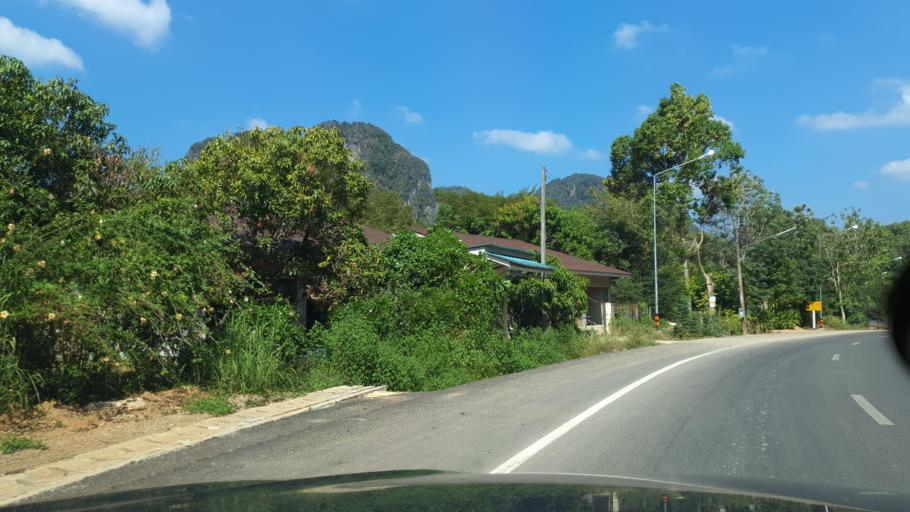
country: TH
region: Krabi
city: Krabi
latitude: 8.0741
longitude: 98.8582
